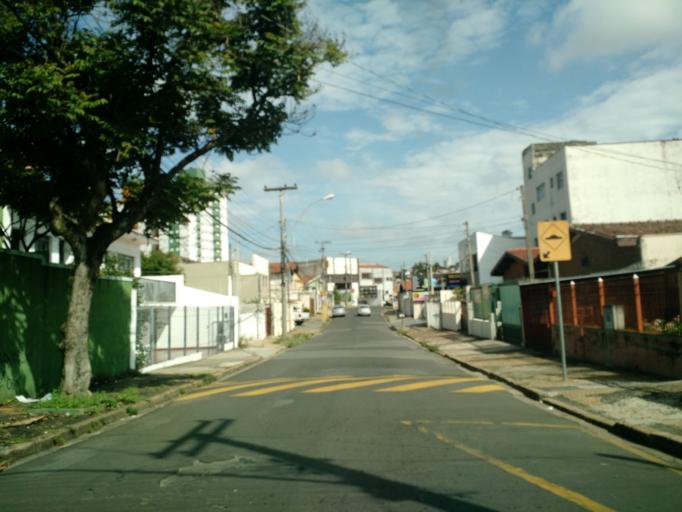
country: BR
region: Sao Paulo
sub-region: Campinas
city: Campinas
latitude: -22.8776
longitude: -47.0347
